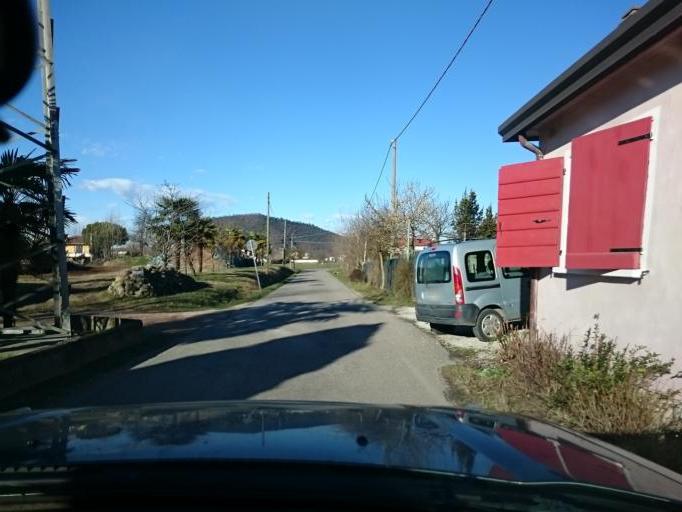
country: IT
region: Veneto
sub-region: Provincia di Padova
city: Torreglia
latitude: 45.3374
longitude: 11.7551
